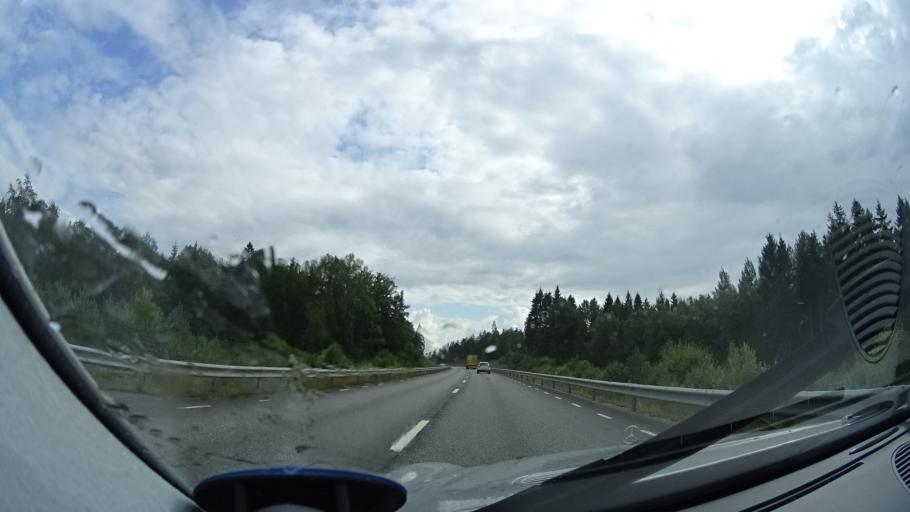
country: SE
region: Blekinge
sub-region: Karlshamns Kommun
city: Svangsta
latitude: 56.3367
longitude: 14.8873
